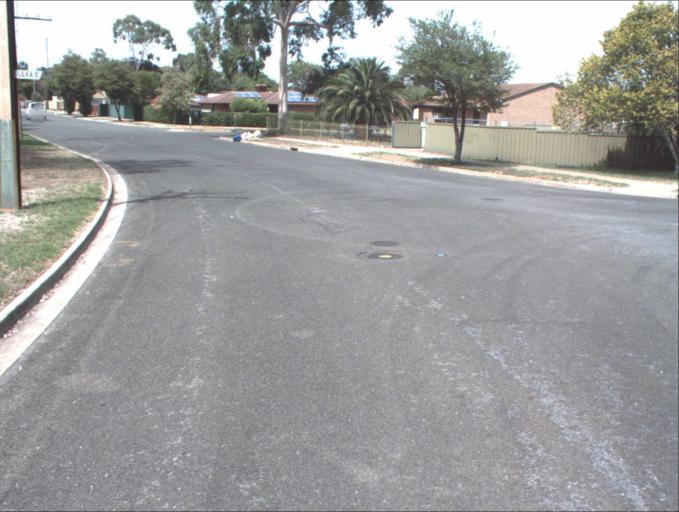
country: AU
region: South Australia
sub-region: Port Adelaide Enfield
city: Enfield
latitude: -34.8456
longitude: 138.6068
